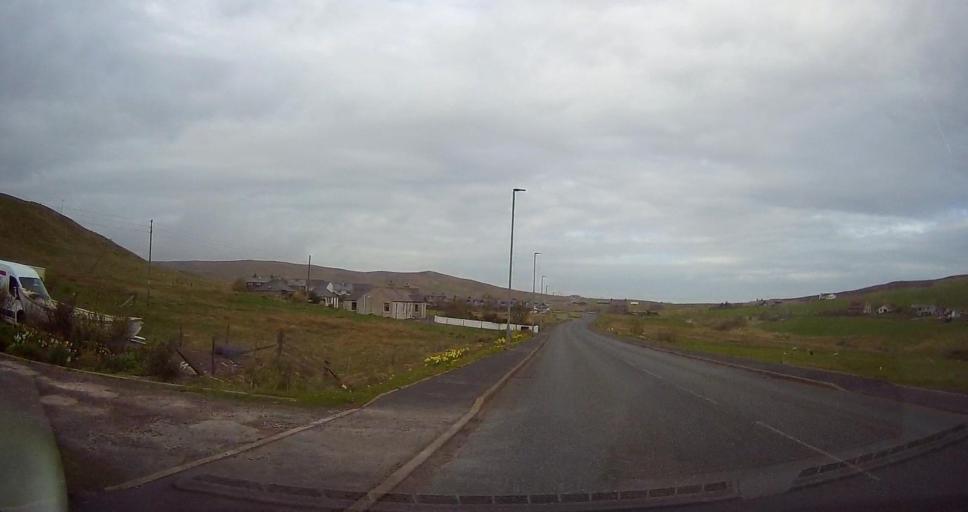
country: GB
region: Scotland
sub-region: Shetland Islands
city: Sandwick
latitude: 60.0505
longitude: -1.2269
